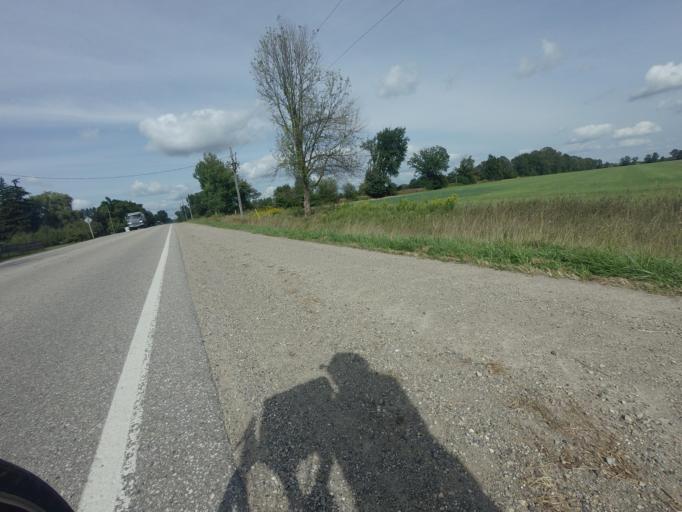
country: CA
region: Ontario
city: Waterloo
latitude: 43.5895
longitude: -80.4649
